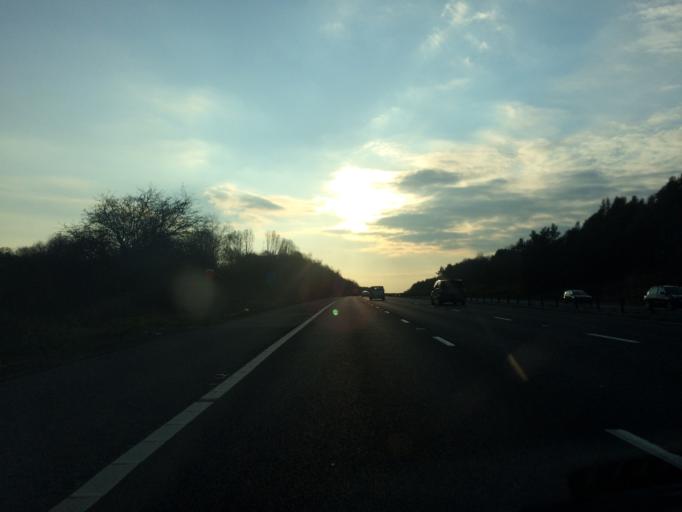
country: GB
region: England
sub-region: Wiltshire
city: Chippenham
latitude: 51.5144
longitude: -2.0841
